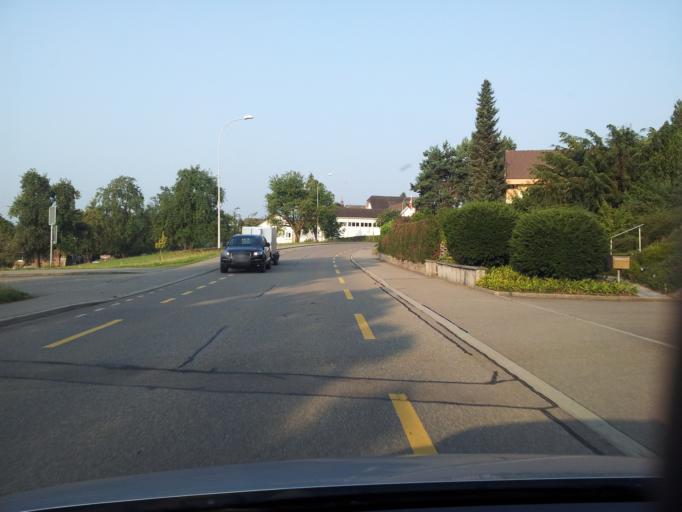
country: CH
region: Lucerne
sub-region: Sursee District
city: Sursee
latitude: 47.1744
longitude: 8.1234
